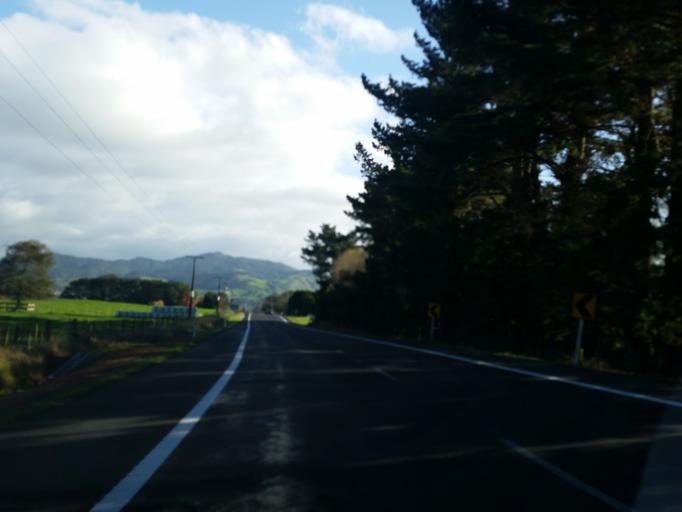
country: NZ
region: Waikato
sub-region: Hauraki District
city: Waihi
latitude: -37.4117
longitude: 175.8631
